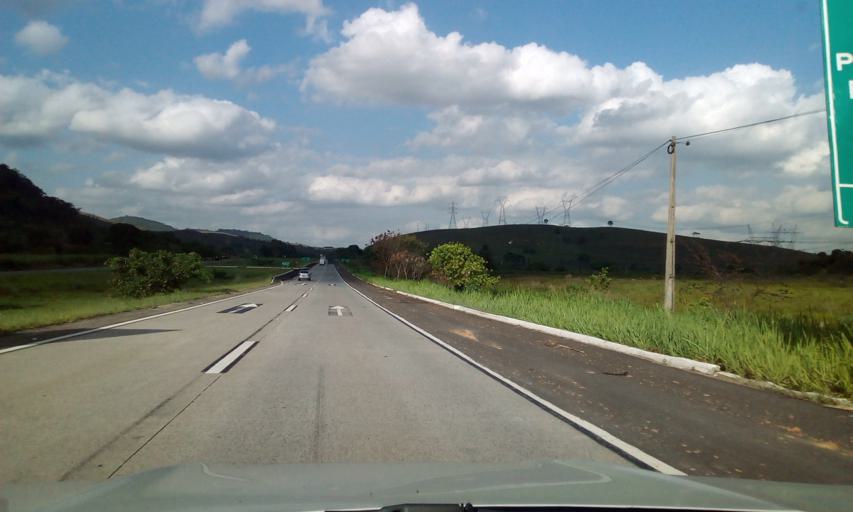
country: BR
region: Pernambuco
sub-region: Joaquim Nabuco
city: Joaquim Nabuco
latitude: -8.6008
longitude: -35.5307
